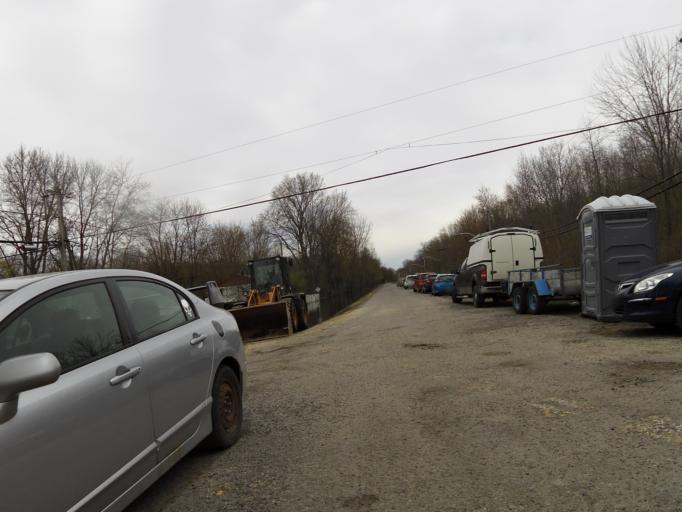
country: CA
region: Quebec
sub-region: Laurentides
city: Sainte-Marthe-sur-le-Lac
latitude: 45.5157
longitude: -73.9571
